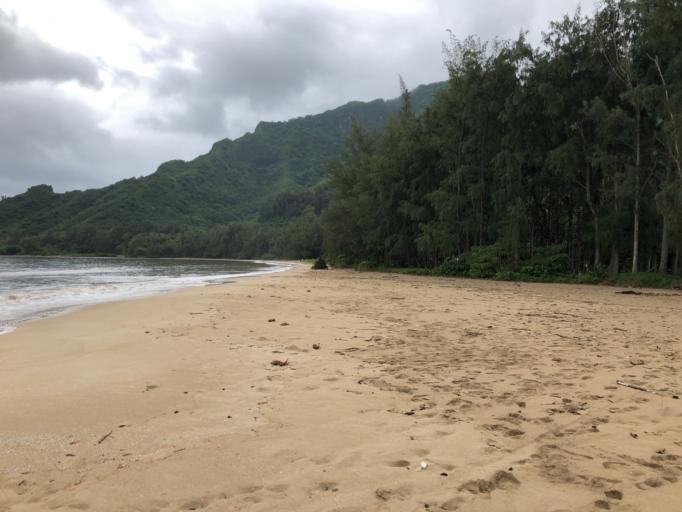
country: US
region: Hawaii
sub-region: Honolulu County
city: Punalu'u
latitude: 21.5563
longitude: -157.8746
